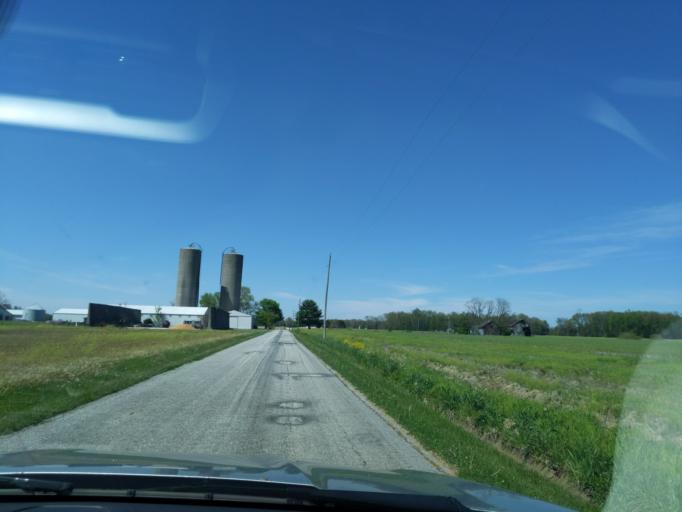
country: US
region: Indiana
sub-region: Decatur County
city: Greensburg
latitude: 39.2413
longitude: -85.4336
